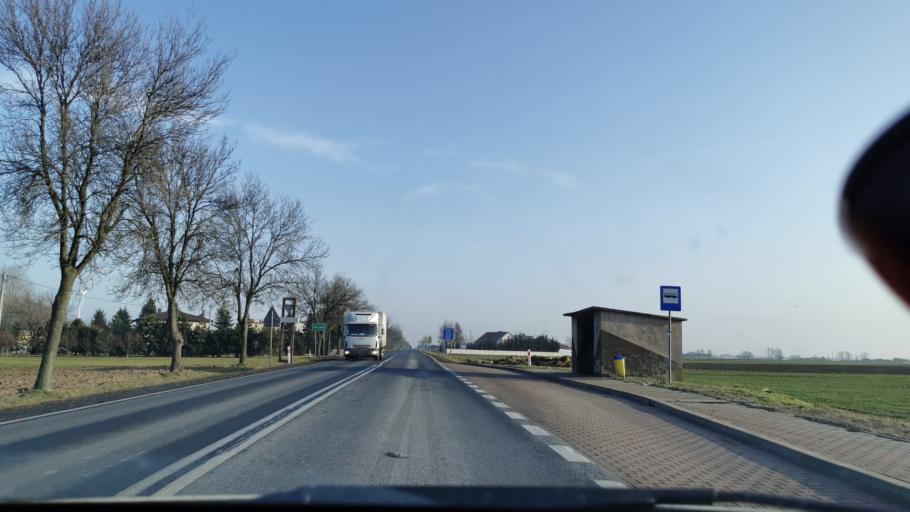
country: PL
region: Lodz Voivodeship
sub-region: Powiat sieradzki
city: Blaszki
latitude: 51.6756
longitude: 18.3585
